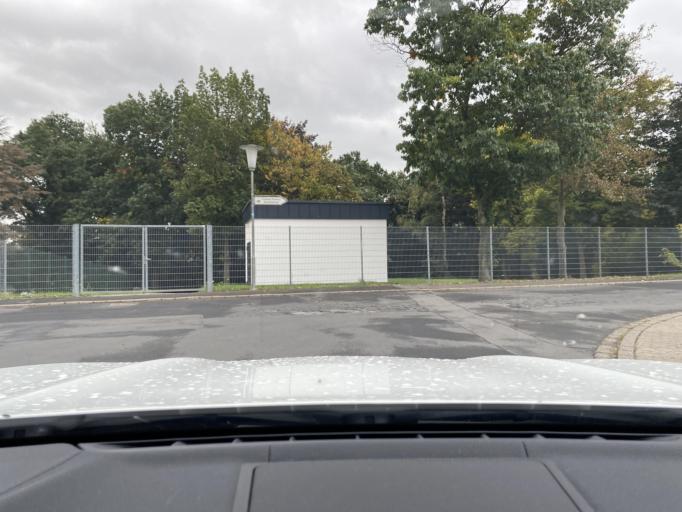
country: DE
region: Rheinland-Pfalz
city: Saffig
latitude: 50.3929
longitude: 7.4065
